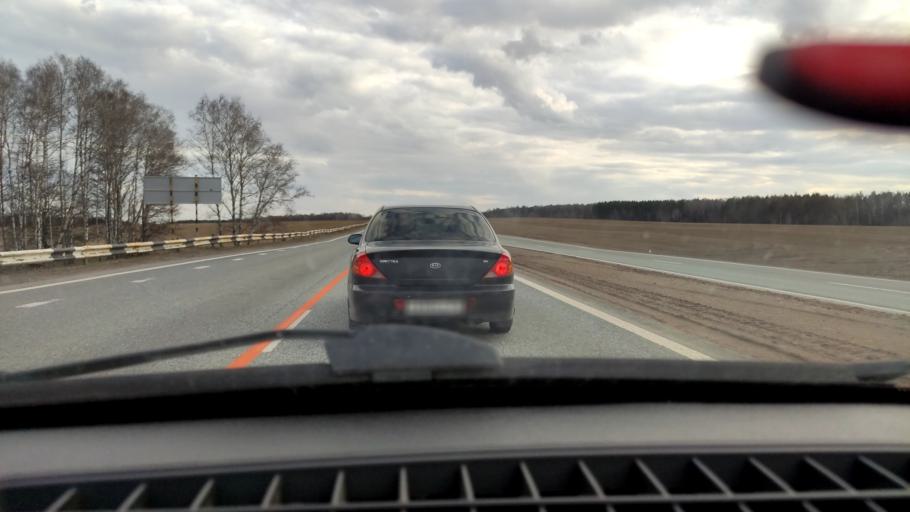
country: RU
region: Bashkortostan
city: Tolbazy
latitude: 54.1152
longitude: 55.9005
